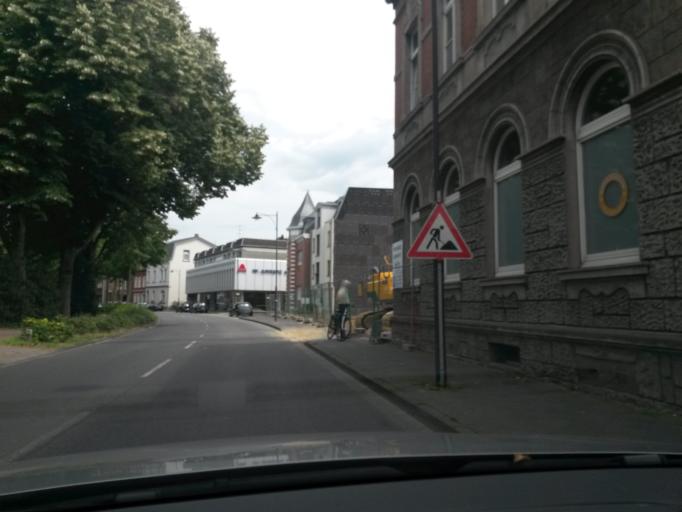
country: DE
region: North Rhine-Westphalia
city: Kempen
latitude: 51.3621
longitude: 6.4198
